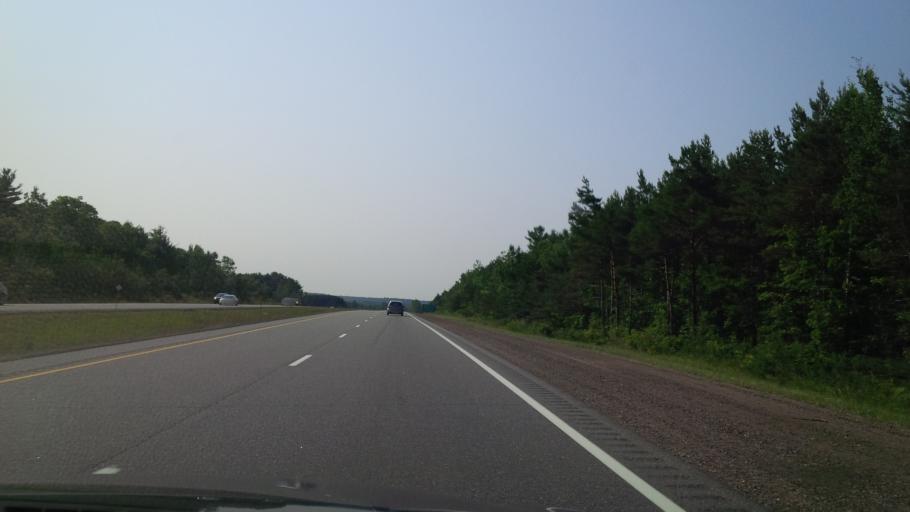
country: CA
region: Ontario
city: Bracebridge
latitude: 45.0601
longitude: -79.2956
